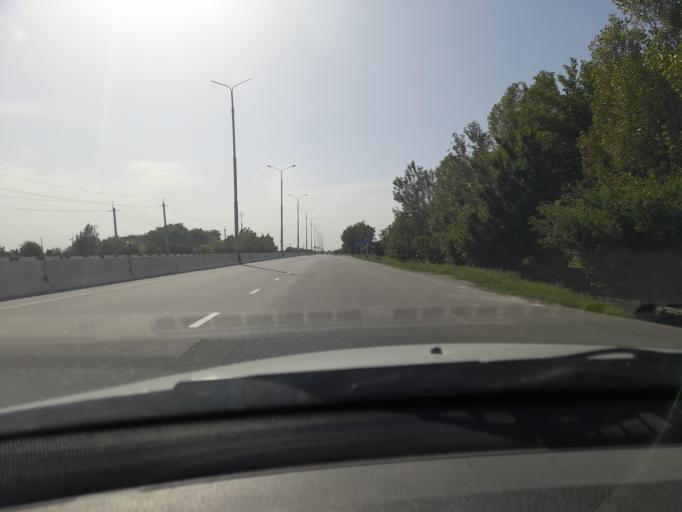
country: UZ
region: Samarqand
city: Ishtixon
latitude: 39.9563
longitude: 66.4779
